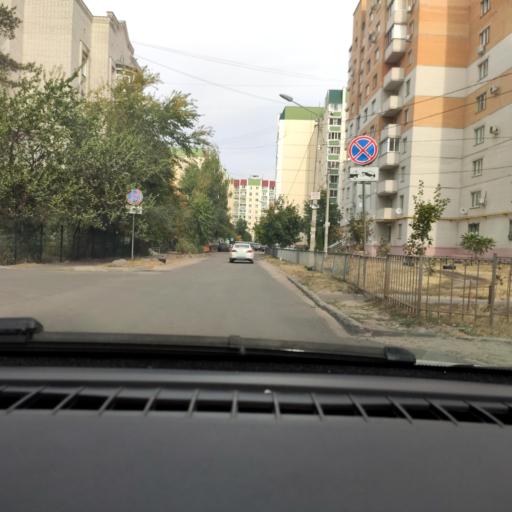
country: RU
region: Voronezj
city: Podgornoye
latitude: 51.7182
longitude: 39.1669
